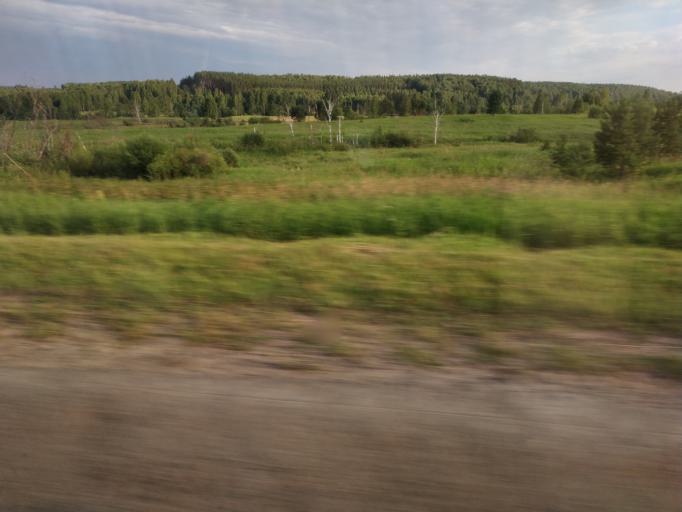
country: RU
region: Sverdlovsk
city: Kamyshlov
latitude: 57.0137
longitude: 62.7180
